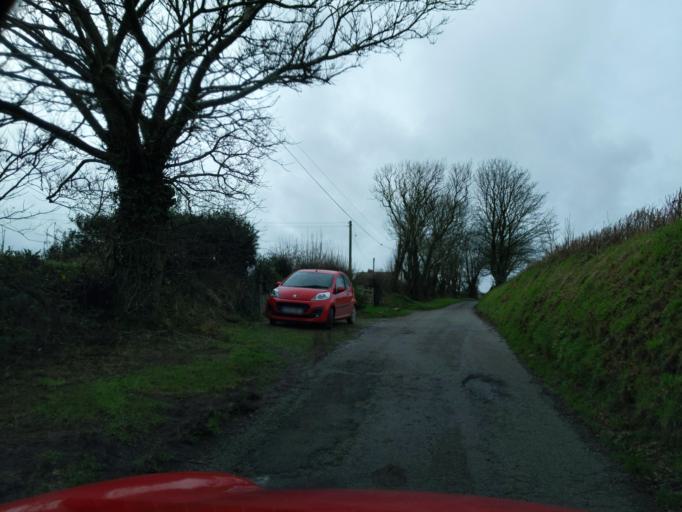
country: GB
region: England
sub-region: Cornwall
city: Duloe
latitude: 50.3496
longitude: -4.5507
